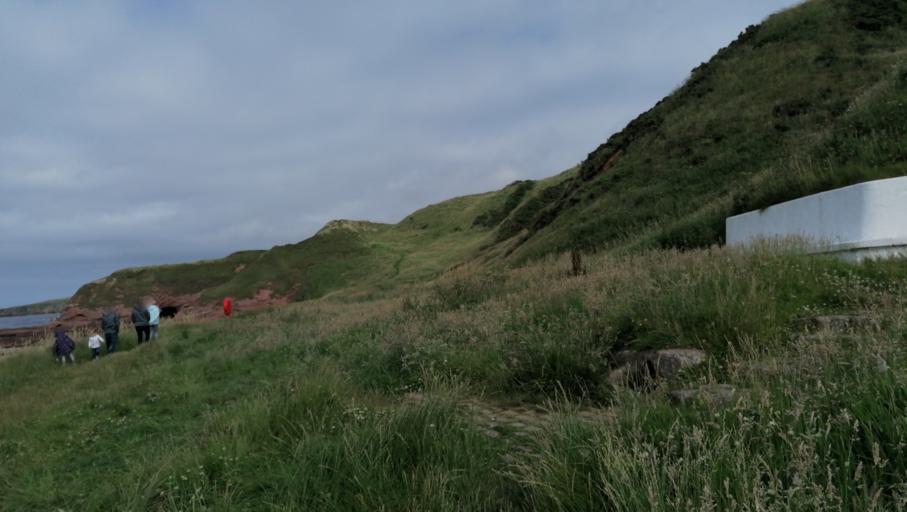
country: GB
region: Scotland
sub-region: Aberdeenshire
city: Rosehearty
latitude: 57.6710
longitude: -2.1914
